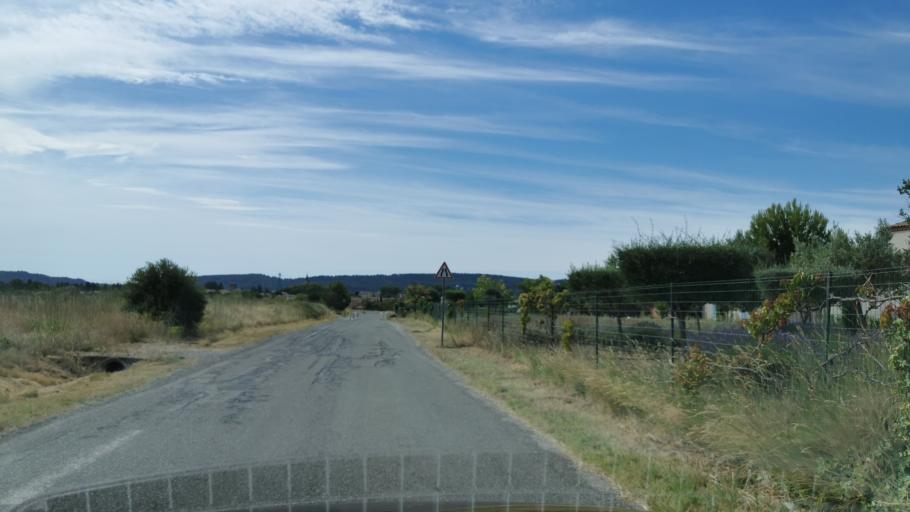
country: FR
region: Languedoc-Roussillon
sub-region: Departement de l'Herault
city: Olonzac
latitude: 43.2743
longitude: 2.7110
